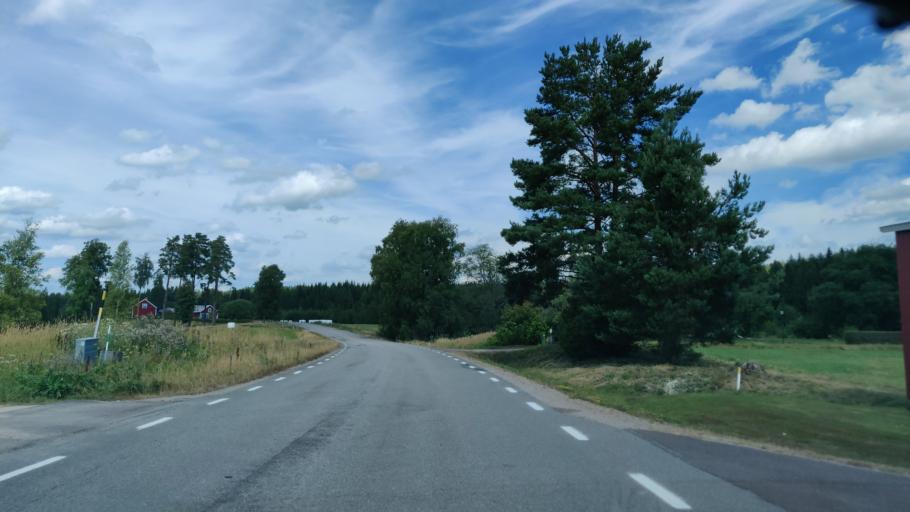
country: SE
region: Vaermland
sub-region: Hagfors Kommun
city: Ekshaerad
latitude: 60.0910
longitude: 13.5094
